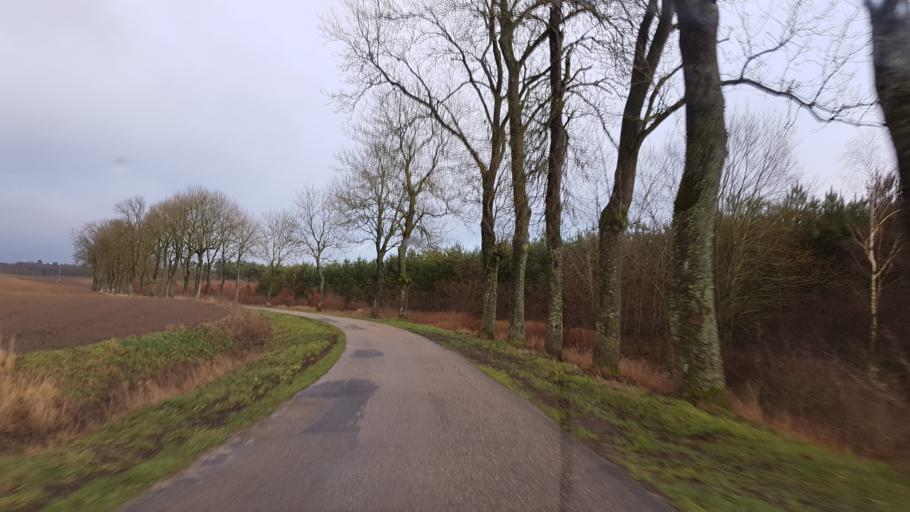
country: PL
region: West Pomeranian Voivodeship
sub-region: Powiat swidwinski
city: Rabino
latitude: 53.9400
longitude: 15.9413
